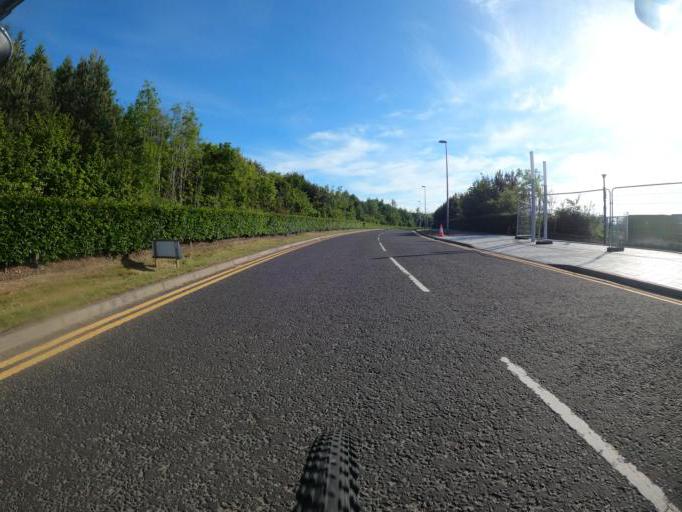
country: GB
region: Scotland
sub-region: Midlothian
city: Loanhead
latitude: 55.9188
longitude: -3.1286
